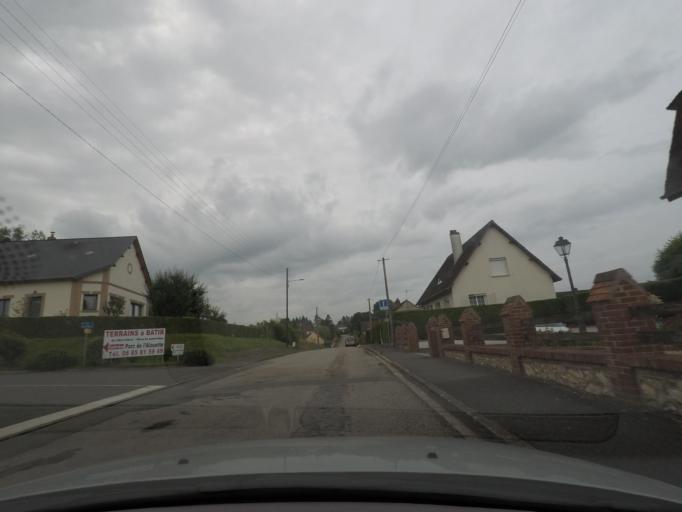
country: FR
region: Haute-Normandie
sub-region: Departement de la Seine-Maritime
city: Neufchatel-en-Bray
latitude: 49.7294
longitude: 1.4427
